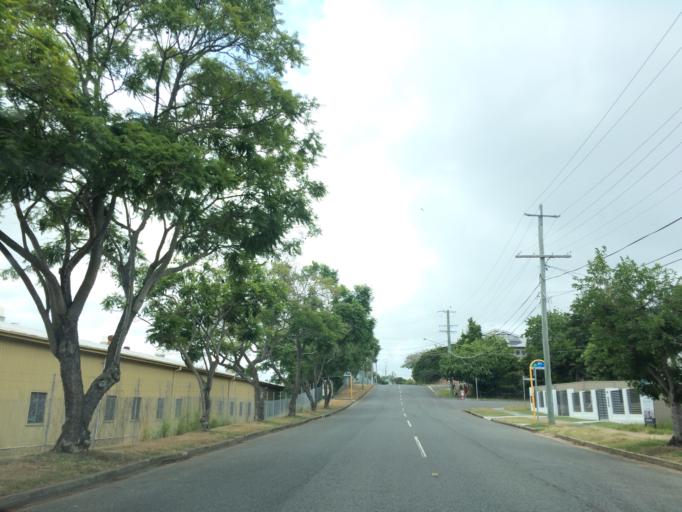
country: AU
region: Queensland
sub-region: Brisbane
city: Balmoral
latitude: -27.4457
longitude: 153.0634
